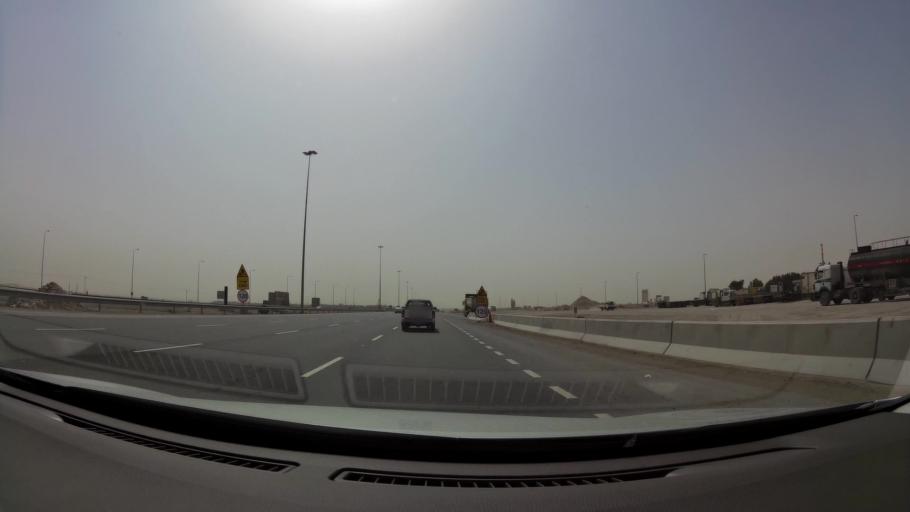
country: QA
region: Baladiyat ar Rayyan
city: Ar Rayyan
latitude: 25.1698
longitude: 51.3190
